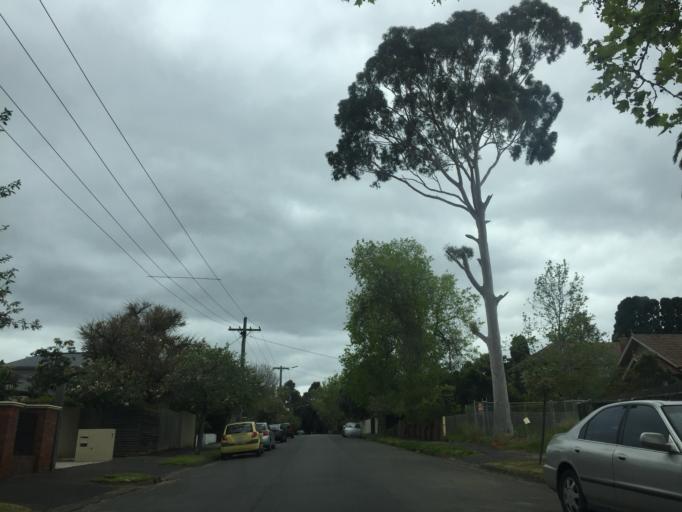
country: AU
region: Victoria
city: Balwyn
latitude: -37.8132
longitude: 145.0570
